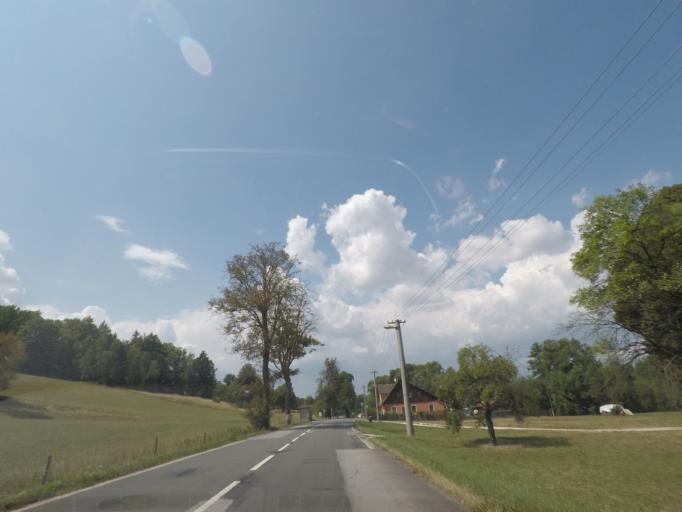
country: CZ
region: Kralovehradecky
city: Zadni Mostek
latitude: 50.5254
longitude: 15.6973
